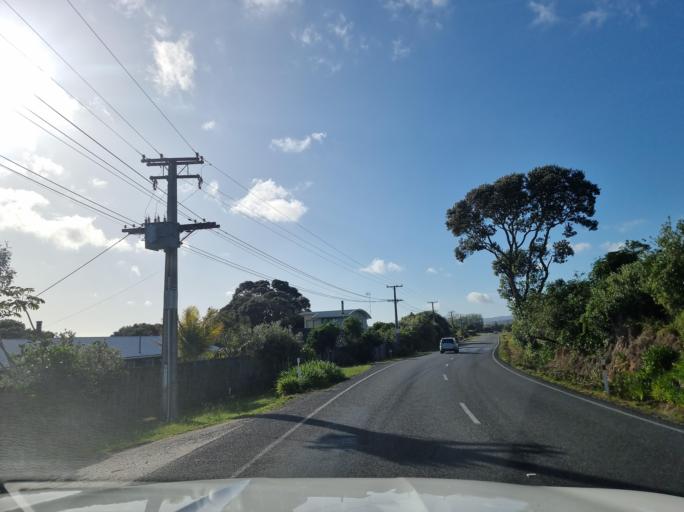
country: NZ
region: Northland
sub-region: Whangarei
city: Ruakaka
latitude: -35.9934
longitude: 174.4709
